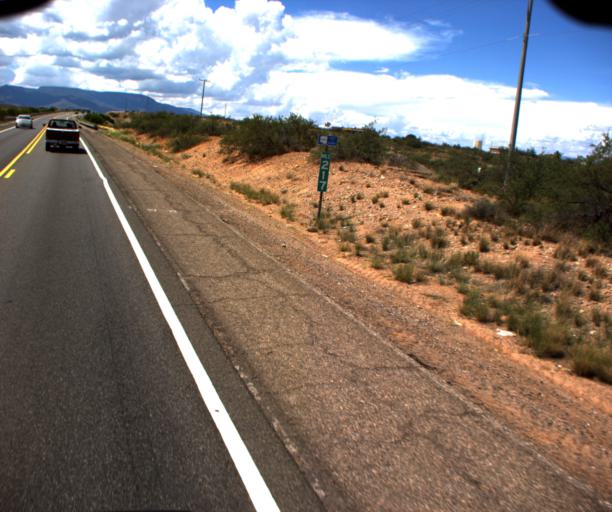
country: US
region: Arizona
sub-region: Yavapai County
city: Camp Verde
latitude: 34.5985
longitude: -111.8976
